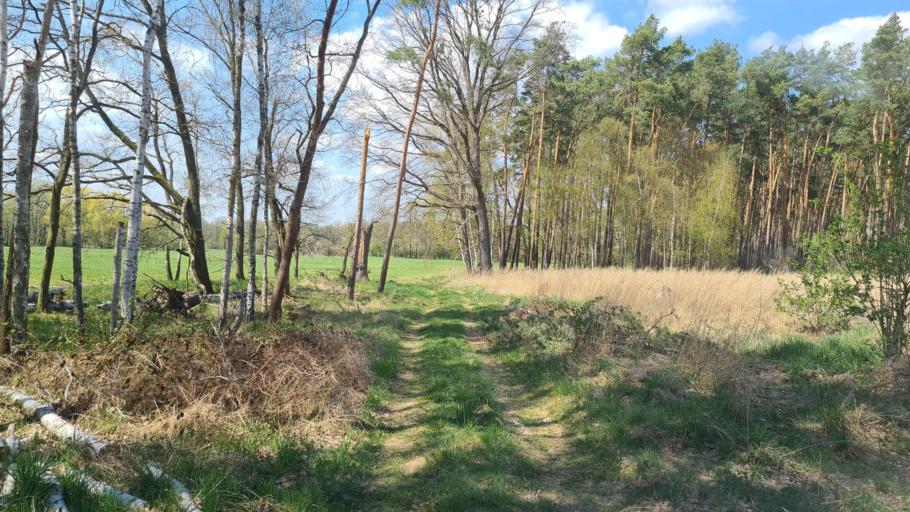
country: DE
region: Brandenburg
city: Finsterwalde
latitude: 51.6716
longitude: 13.6883
